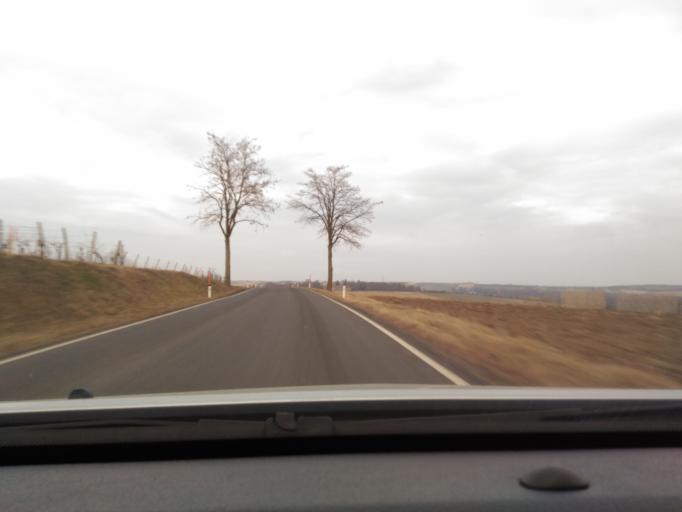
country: AT
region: Lower Austria
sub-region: Politischer Bezirk Mistelbach
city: Drasenhofen
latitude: 48.7441
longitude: 16.6313
